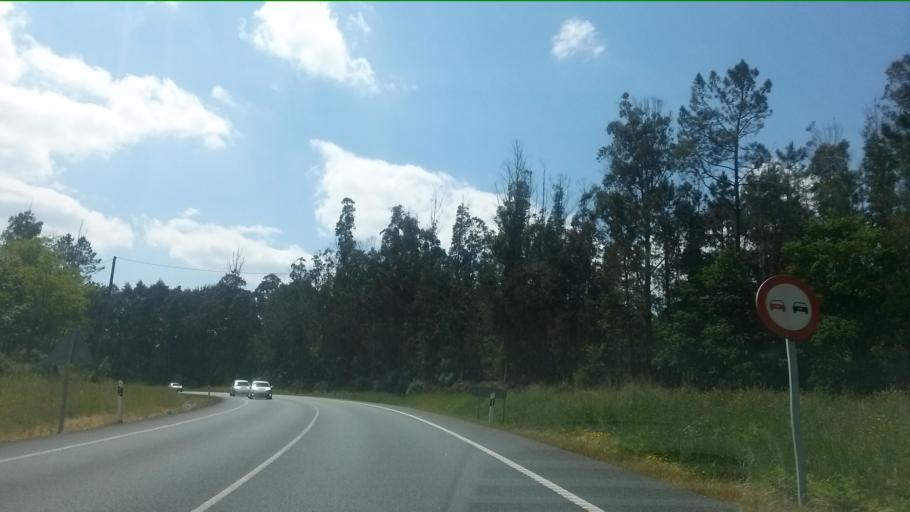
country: ES
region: Galicia
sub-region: Provincia da Coruna
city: Frades
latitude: 42.9658
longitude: -8.3100
